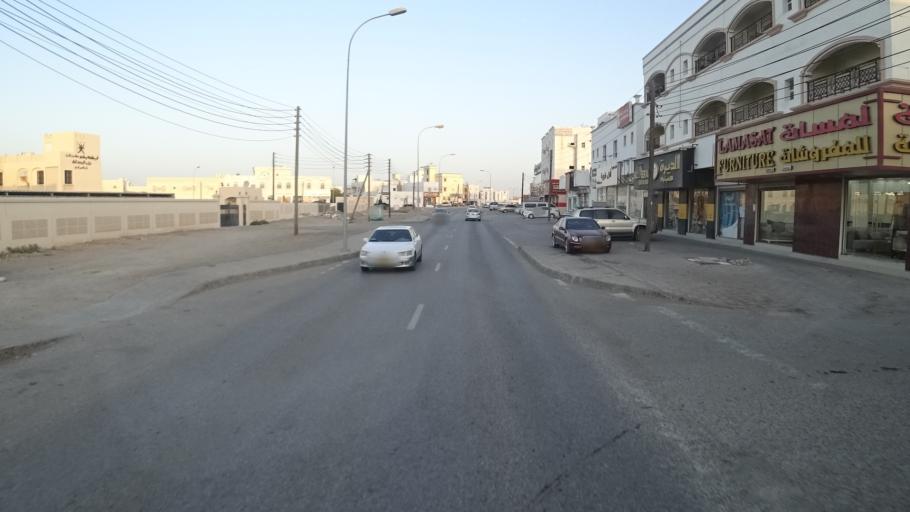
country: OM
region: Ash Sharqiyah
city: Sur
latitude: 22.5805
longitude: 59.5101
